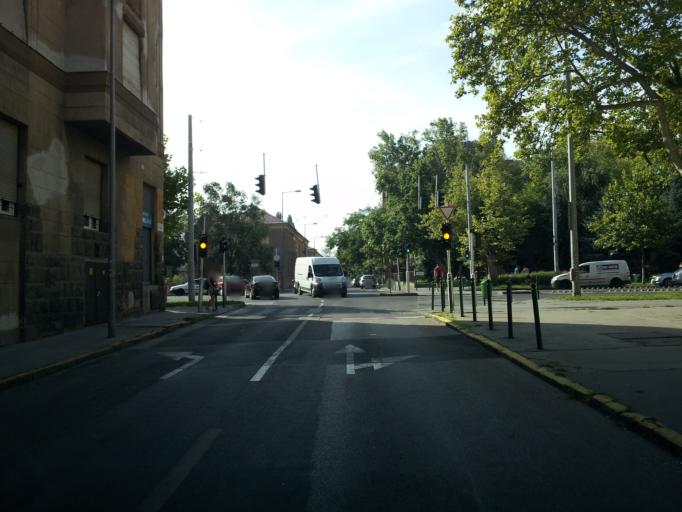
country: HU
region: Budapest
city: Budapest IX. keruelet
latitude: 47.4759
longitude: 19.0730
